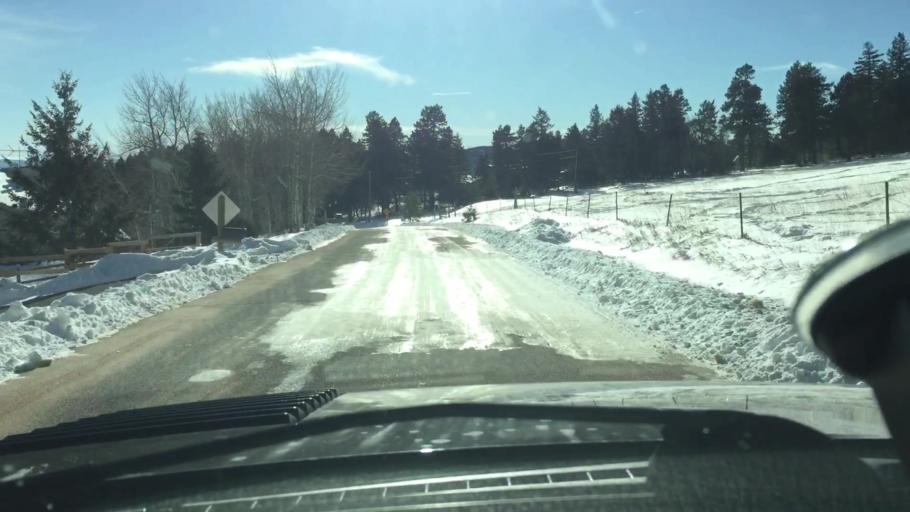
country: US
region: Colorado
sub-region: Jefferson County
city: Indian Hills
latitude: 39.5626
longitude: -105.2531
